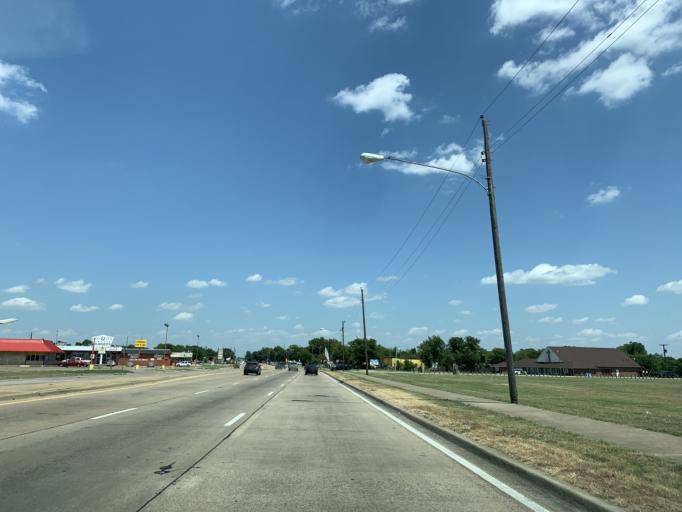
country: US
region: Texas
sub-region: Dallas County
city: Hutchins
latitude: 32.6961
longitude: -96.7672
